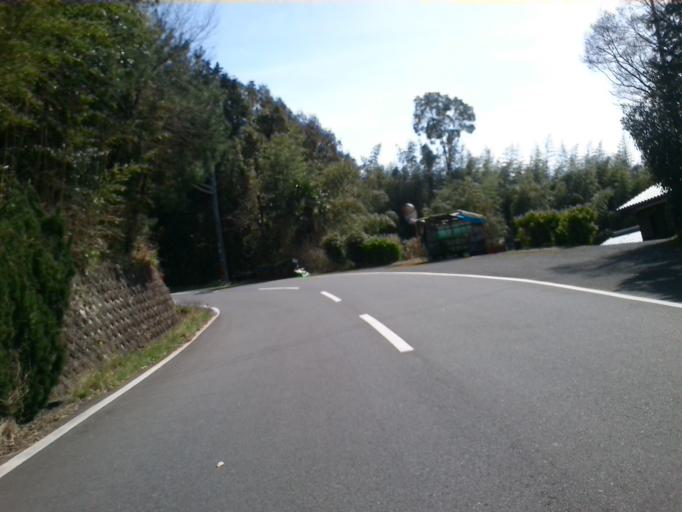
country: JP
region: Nara
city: Nara-shi
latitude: 34.7220
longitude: 135.8669
